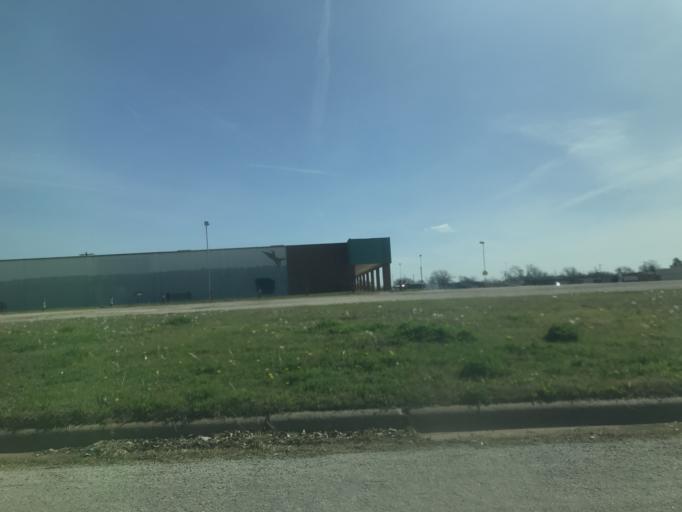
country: US
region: Texas
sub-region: Taylor County
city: Abilene
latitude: 32.4646
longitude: -99.7425
